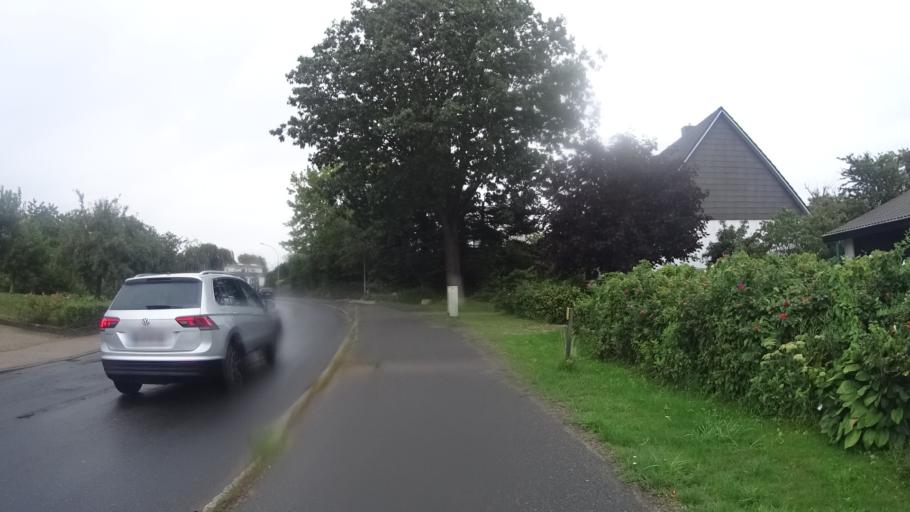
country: DE
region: Schleswig-Holstein
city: Alveslohe
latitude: 53.7844
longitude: 9.9089
